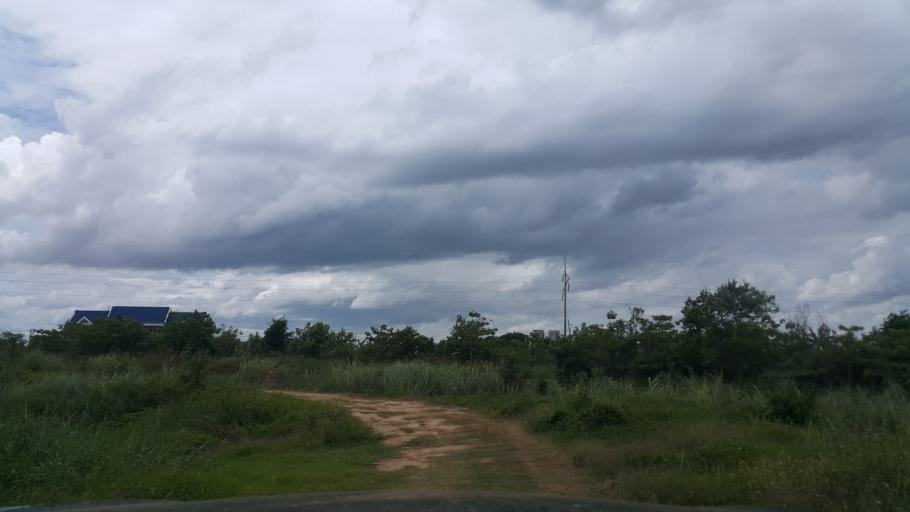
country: TH
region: Sukhothai
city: Sukhothai
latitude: 17.0325
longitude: 99.7994
